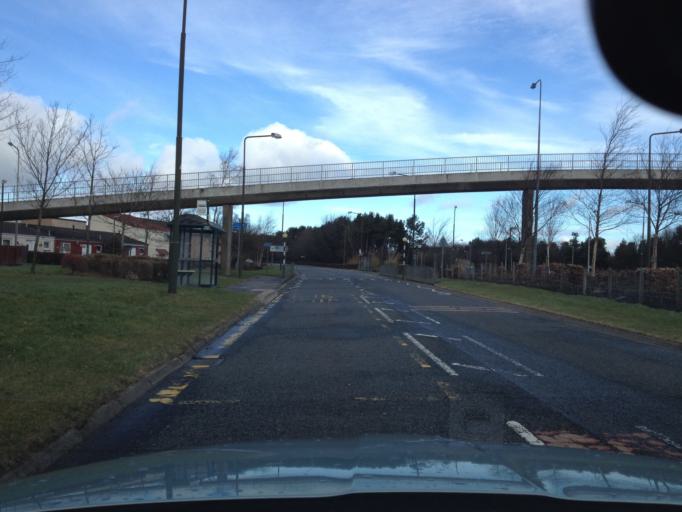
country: GB
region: Scotland
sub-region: West Lothian
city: Livingston
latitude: 55.9079
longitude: -3.5187
